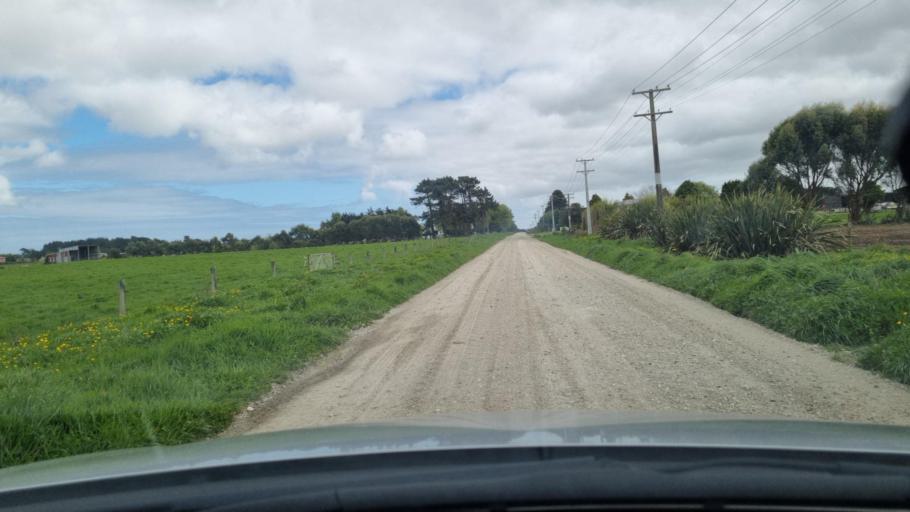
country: NZ
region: Southland
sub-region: Invercargill City
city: Invercargill
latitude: -46.4433
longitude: 168.4101
